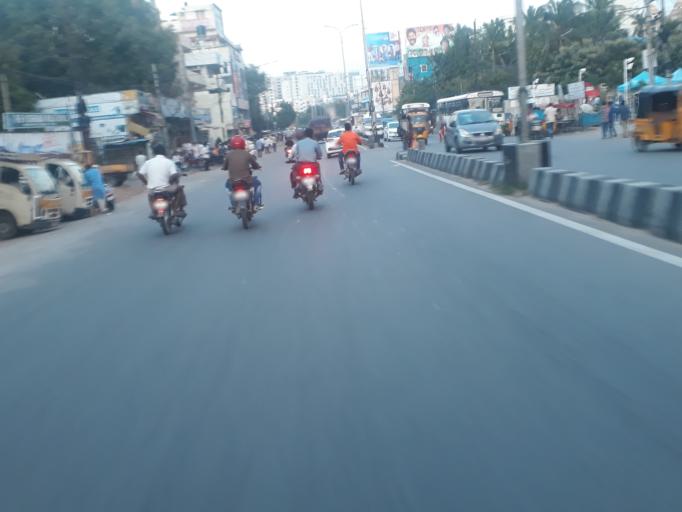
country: IN
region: Telangana
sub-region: Rangareddi
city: Uppal Kalan
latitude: 17.3996
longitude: 78.5374
